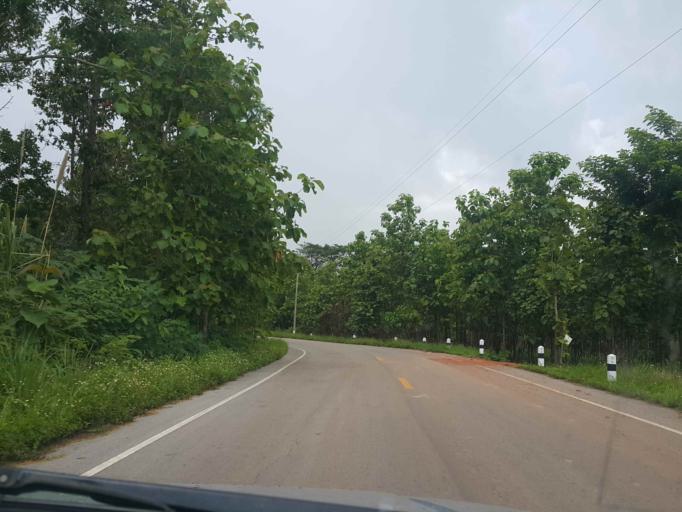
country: TH
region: Phayao
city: Dok Kham Tai
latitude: 19.0442
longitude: 99.9526
